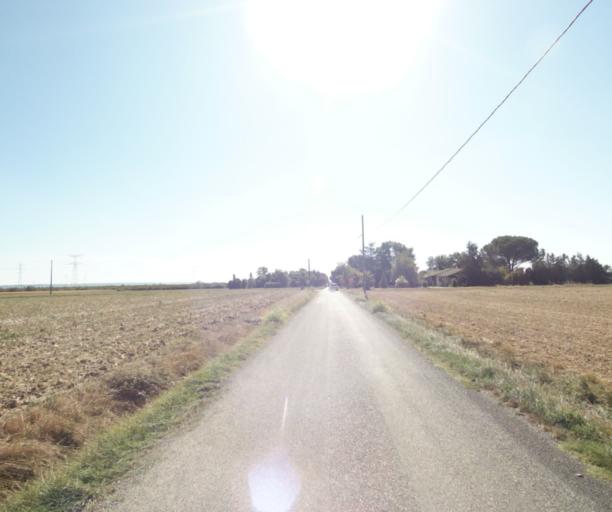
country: FR
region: Midi-Pyrenees
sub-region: Departement du Tarn-et-Garonne
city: Verdun-sur-Garonne
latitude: 43.8353
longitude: 1.2193
